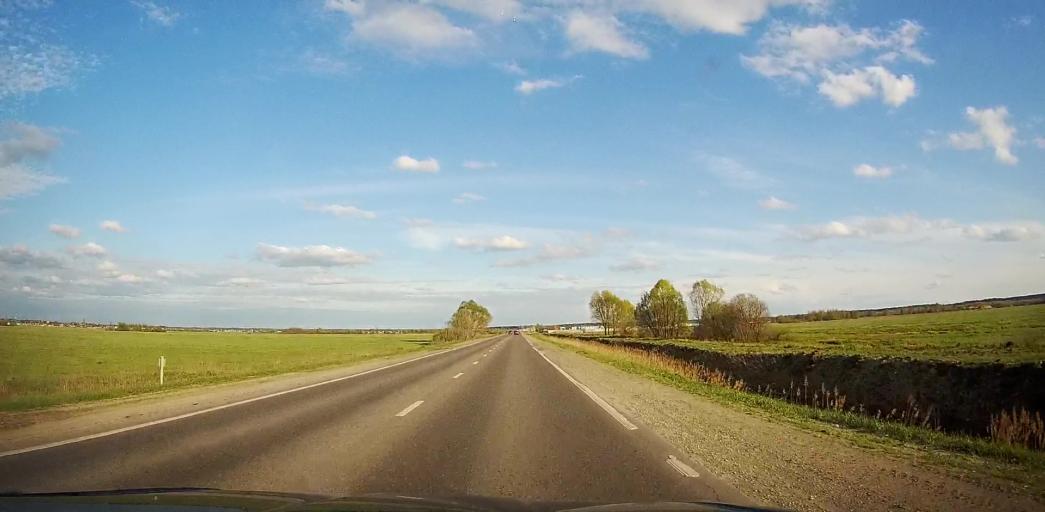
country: RU
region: Moskovskaya
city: Malyshevo
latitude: 55.5015
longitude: 38.2982
